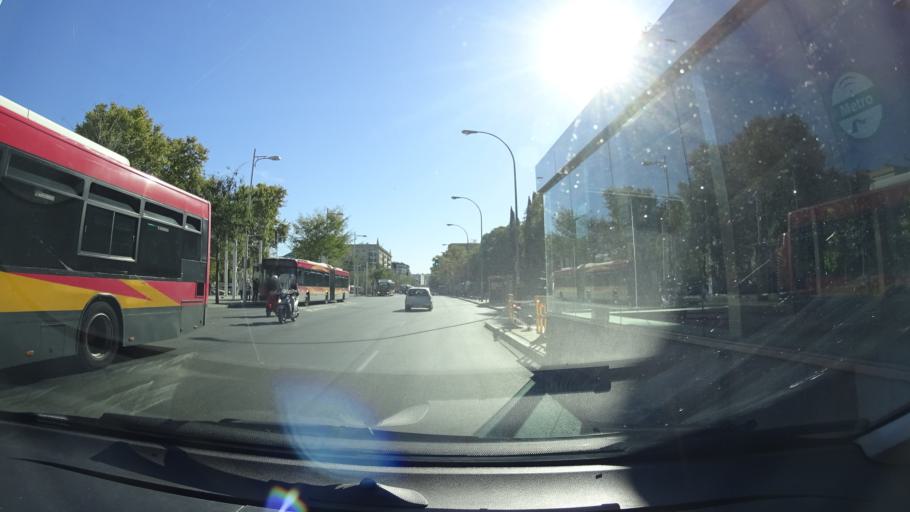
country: ES
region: Andalusia
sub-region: Provincia de Sevilla
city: Sevilla
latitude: 37.3807
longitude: -5.9872
